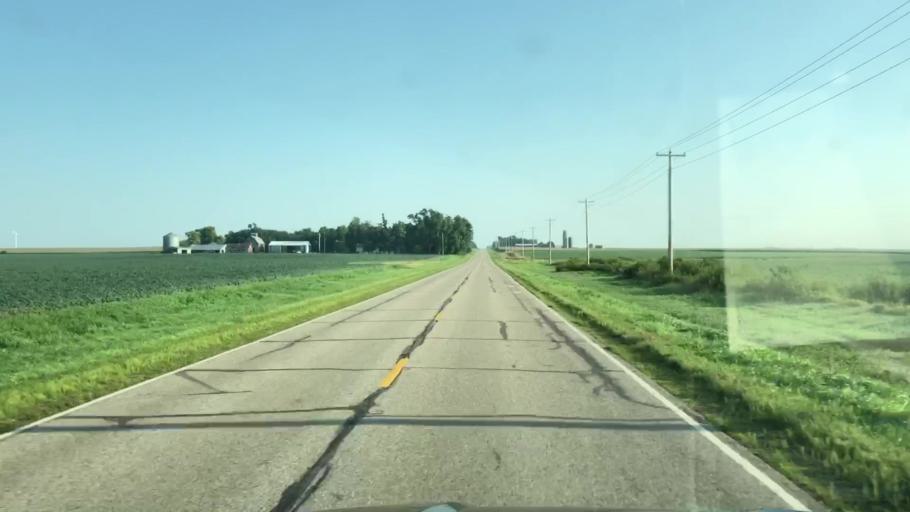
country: US
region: Iowa
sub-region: Lyon County
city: George
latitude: 43.3618
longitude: -95.9983
